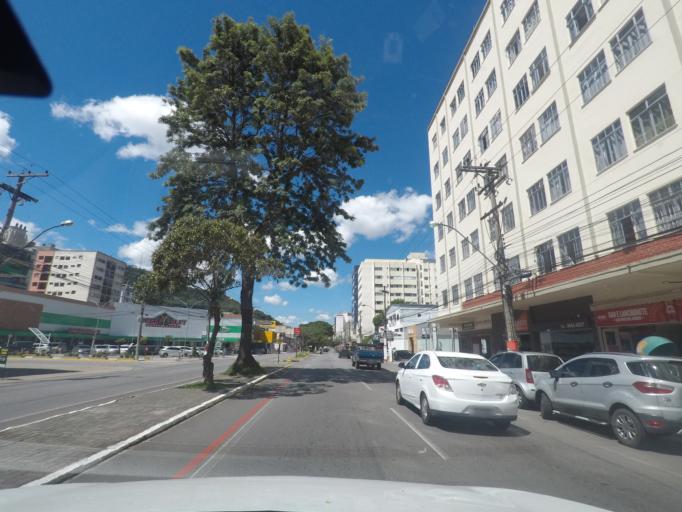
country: BR
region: Rio de Janeiro
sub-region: Teresopolis
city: Teresopolis
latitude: -22.4208
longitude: -42.9754
